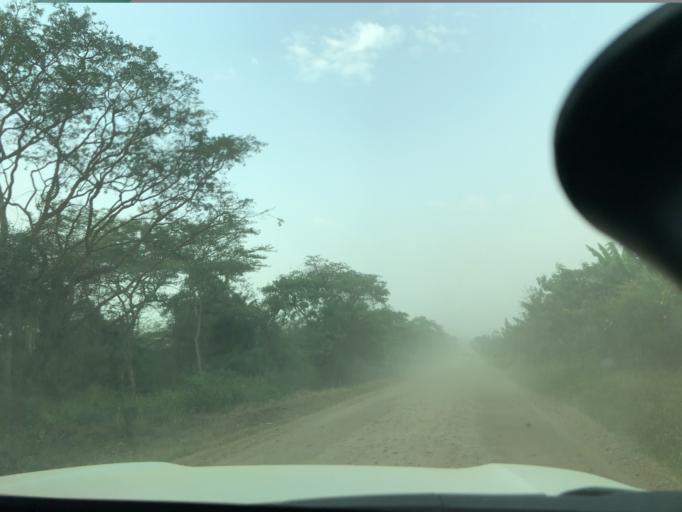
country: CD
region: Nord Kivu
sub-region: North Kivu
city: Butembo
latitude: 0.1531
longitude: 29.6412
